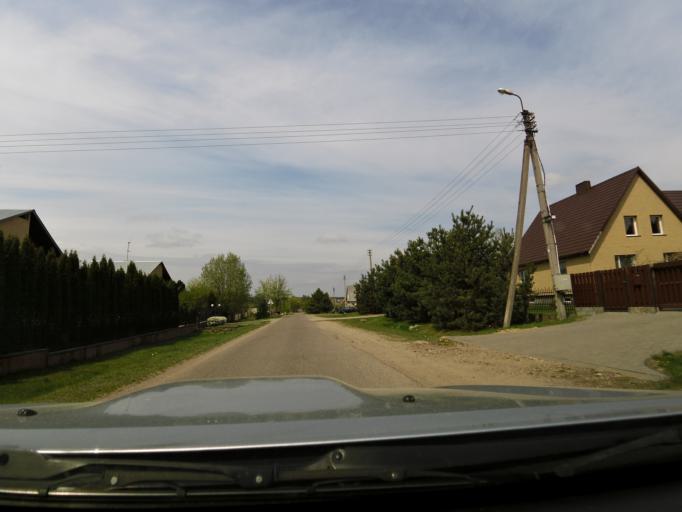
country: LT
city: Salcininkai
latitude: 54.4280
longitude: 25.3130
